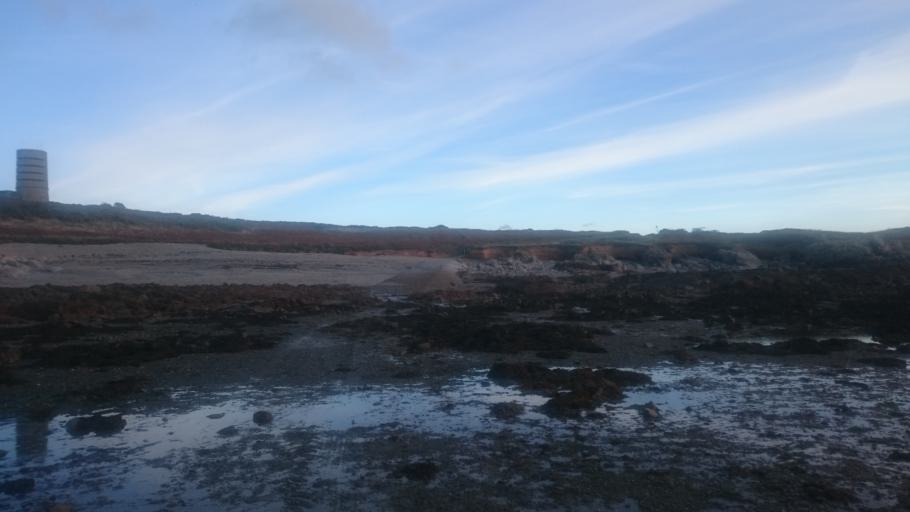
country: GG
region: St Peter Port
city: Saint Peter Port
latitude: 49.4582
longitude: -2.6590
